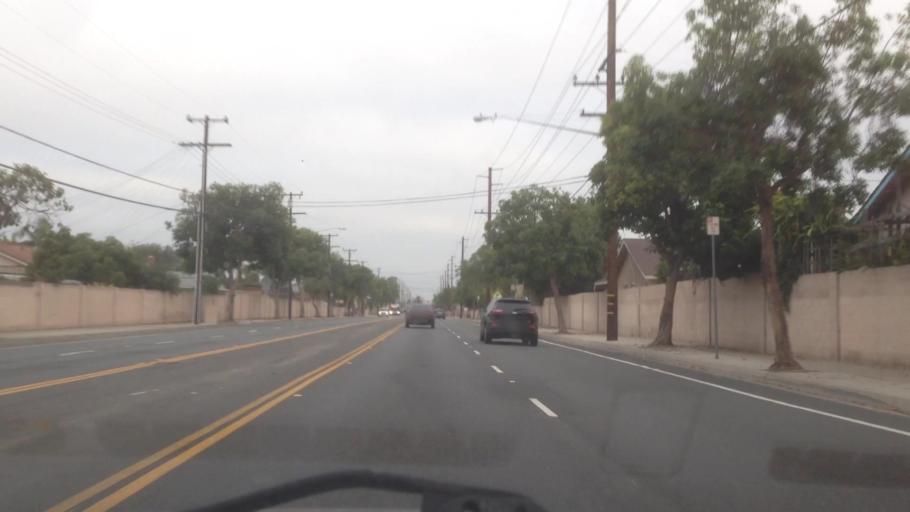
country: US
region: California
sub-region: Orange County
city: Fountain Valley
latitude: 33.7381
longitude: -117.9410
